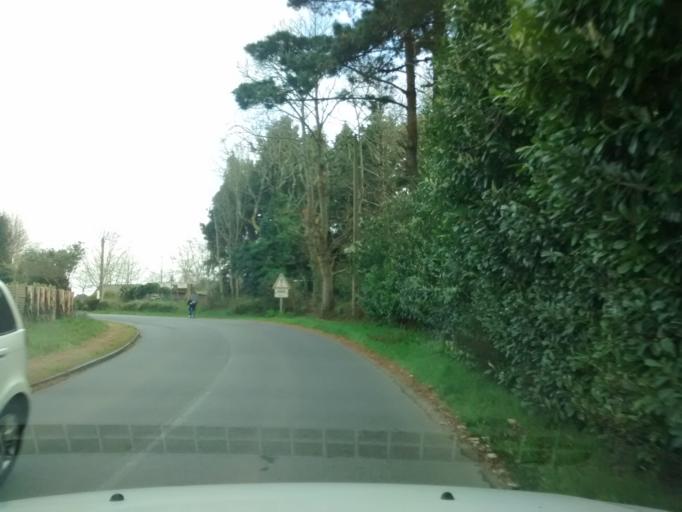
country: FR
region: Brittany
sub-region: Departement du Morbihan
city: Gestel
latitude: 47.7851
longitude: -3.4761
